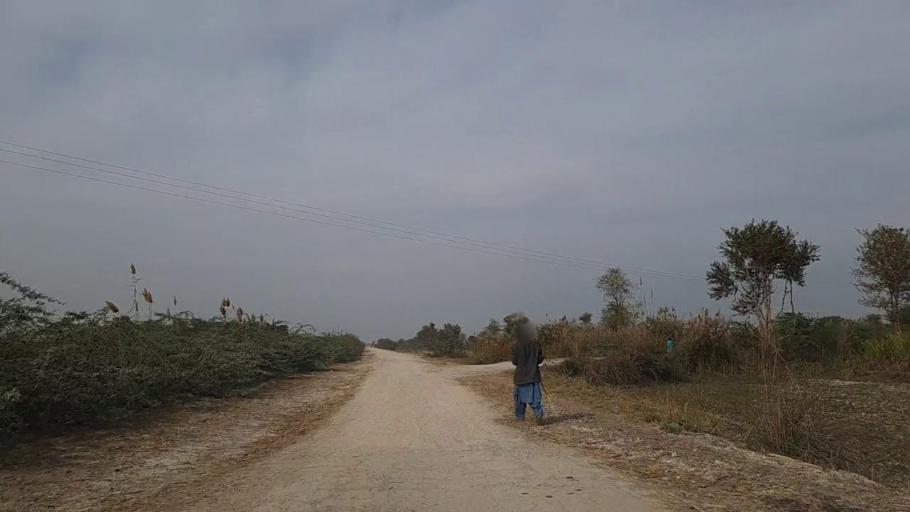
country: PK
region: Sindh
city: Daur
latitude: 26.4079
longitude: 68.4346
